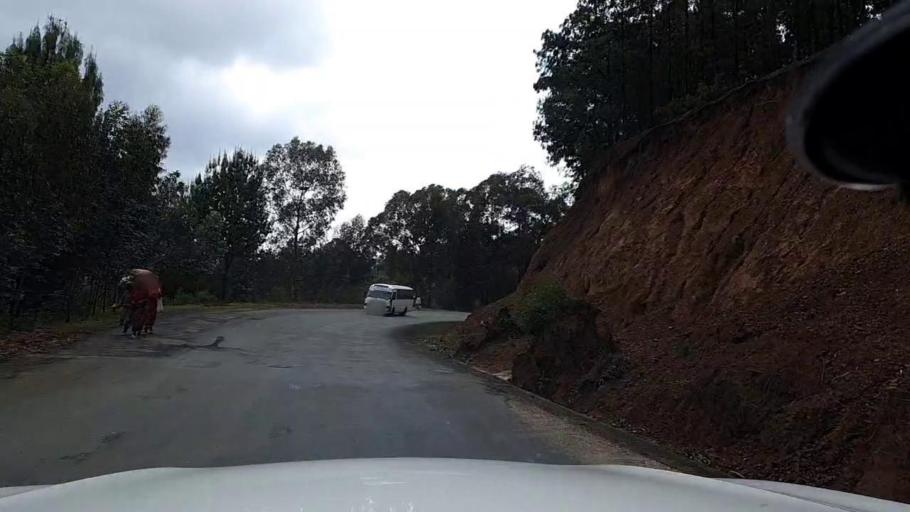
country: RW
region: Western Province
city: Kibuye
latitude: -2.0601
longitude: 29.5281
